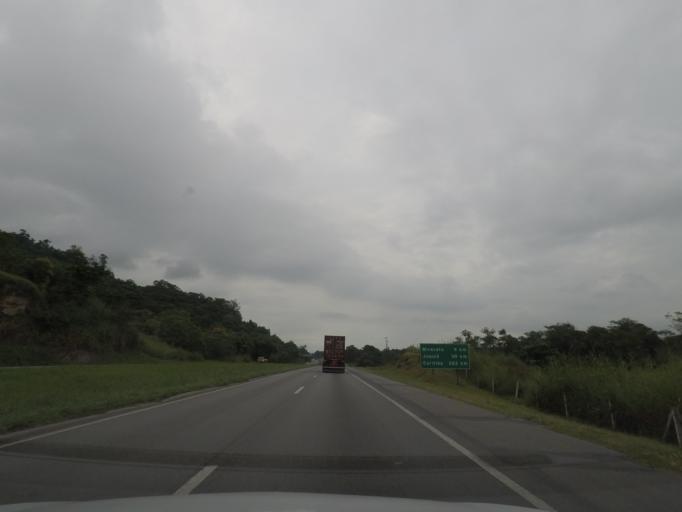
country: BR
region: Sao Paulo
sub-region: Miracatu
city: Miracatu
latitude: -24.2639
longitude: -47.3834
